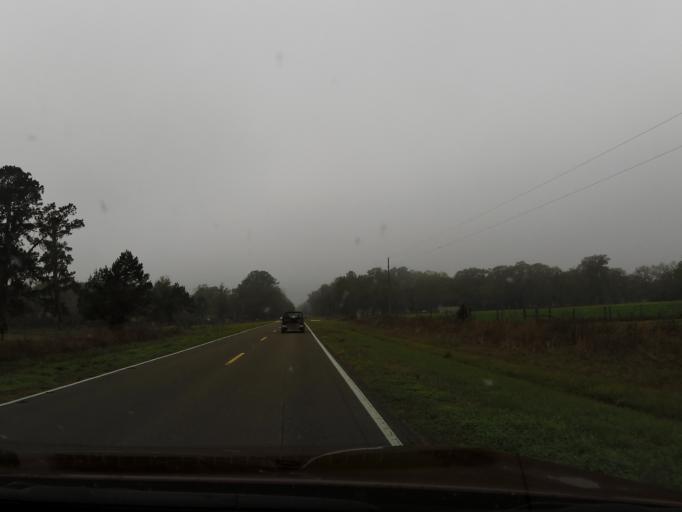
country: US
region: Florida
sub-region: Alachua County
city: Alachua
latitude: 29.8996
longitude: -82.4394
